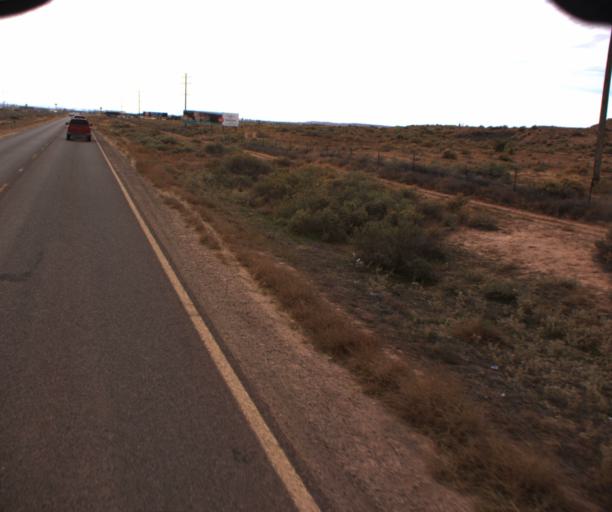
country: US
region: Arizona
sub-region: Apache County
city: Chinle
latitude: 36.1755
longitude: -109.5887
